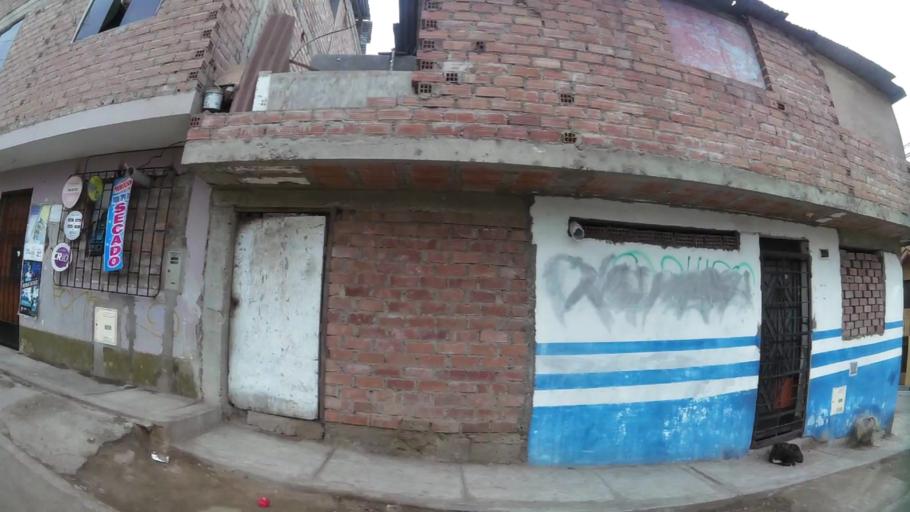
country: PE
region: Lima
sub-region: Lima
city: Surco
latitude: -12.1843
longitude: -76.9544
